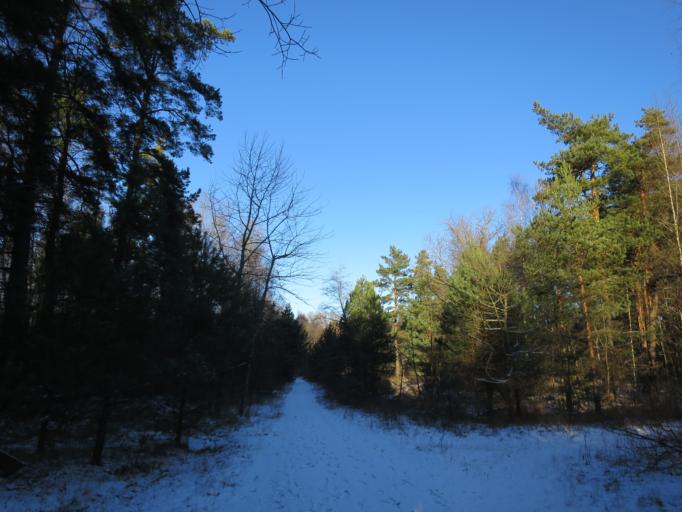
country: LV
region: Riga
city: Bolderaja
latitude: 57.0676
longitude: 24.0656
